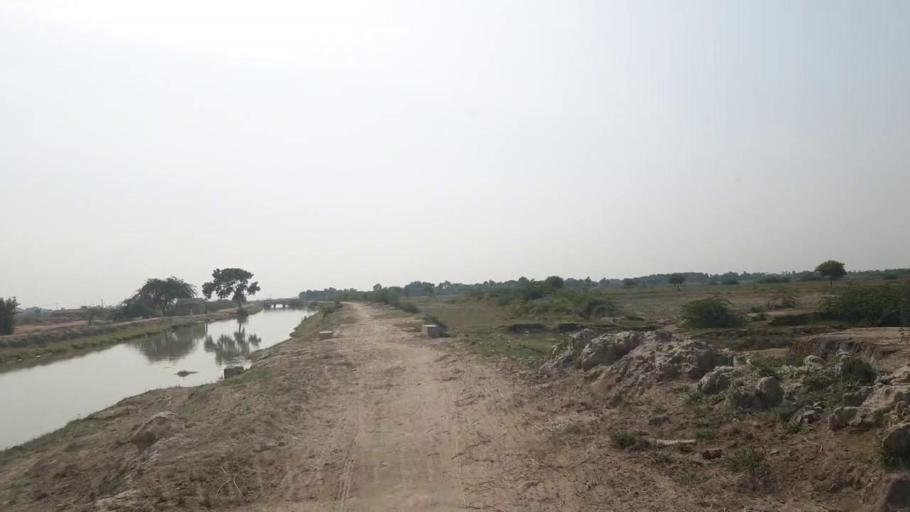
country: PK
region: Sindh
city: Badin
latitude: 24.5566
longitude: 68.8495
